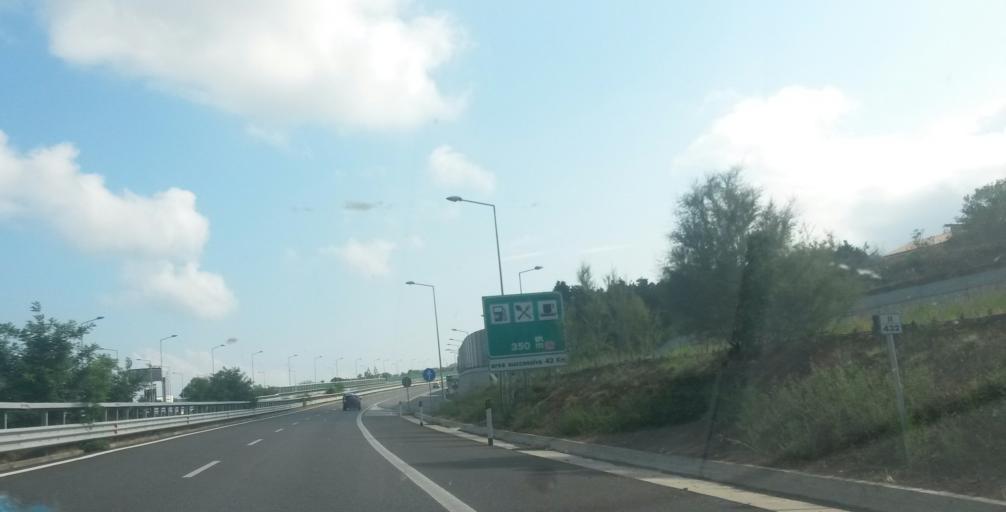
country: IT
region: Calabria
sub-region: Provincia di Reggio Calabria
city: Campo Calabro
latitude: 38.2055
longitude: 15.6408
